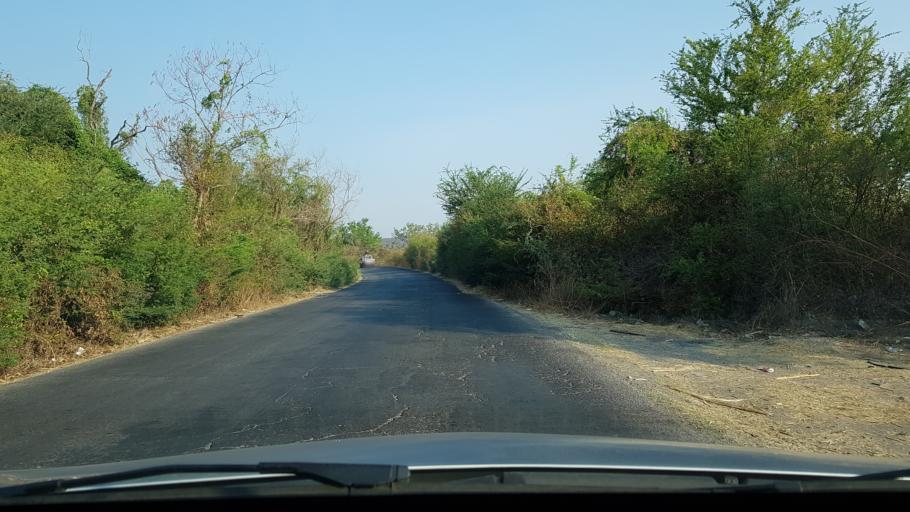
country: MX
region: Morelos
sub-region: Tepalcingo
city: Zacapalco
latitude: 18.6508
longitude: -99.0297
